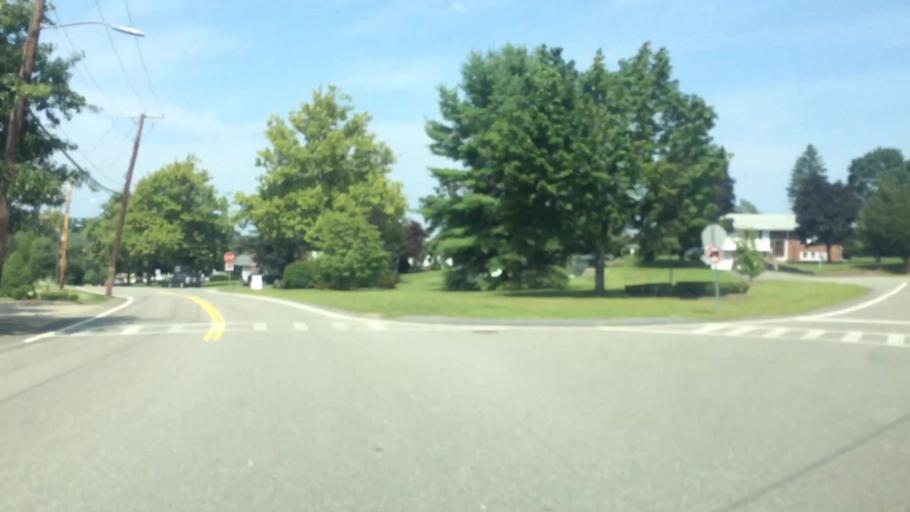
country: US
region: Massachusetts
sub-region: Norfolk County
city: Dedham
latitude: 42.2676
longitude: -71.1845
